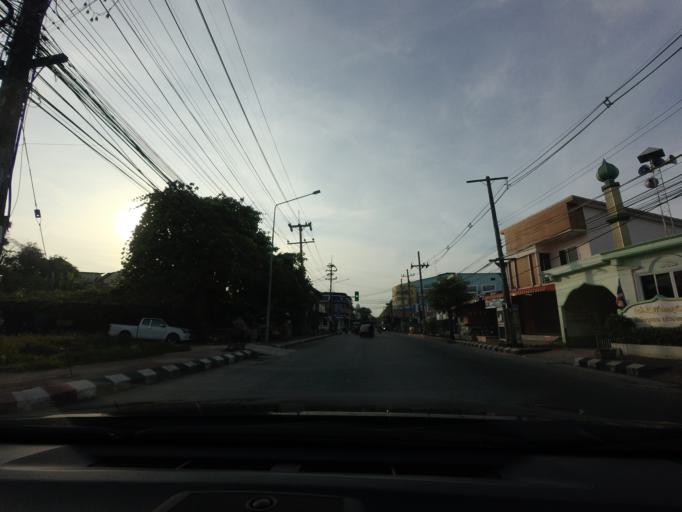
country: TH
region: Narathiwat
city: Narathiwat
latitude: 6.4241
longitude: 101.8280
